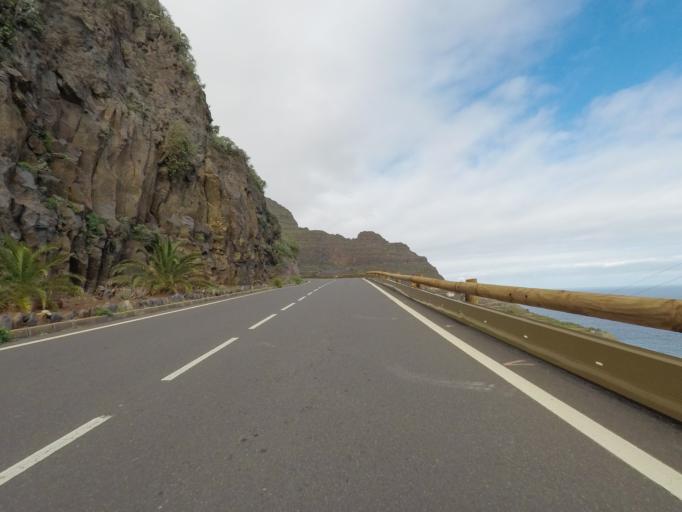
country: ES
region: Canary Islands
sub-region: Provincia de Santa Cruz de Tenerife
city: Agulo
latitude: 28.1847
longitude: -17.1881
